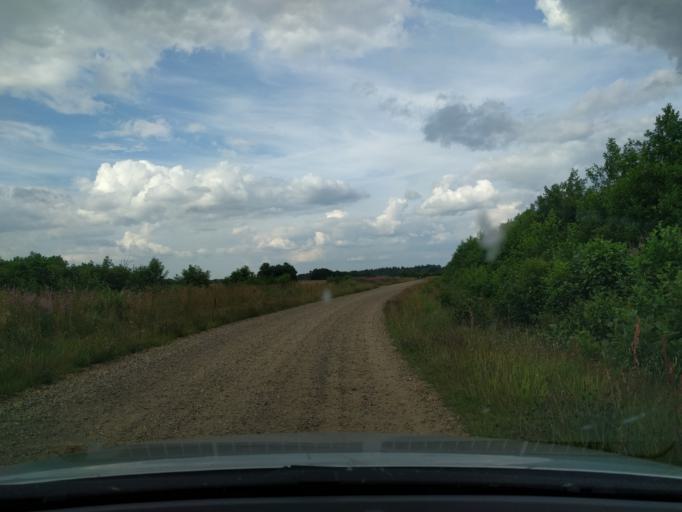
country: DK
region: Central Jutland
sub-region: Herning Kommune
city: Kibaek
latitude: 56.0696
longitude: 8.8852
